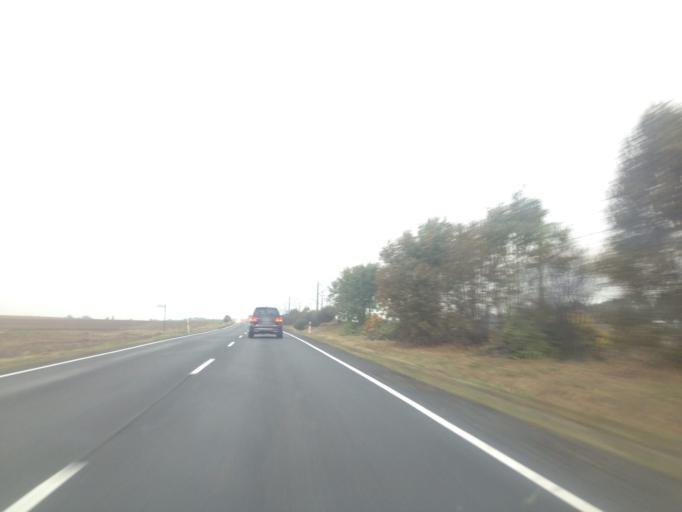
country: PL
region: Greater Poland Voivodeship
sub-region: Powiat gnieznienski
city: Trzemeszno
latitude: 52.5996
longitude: 17.8950
